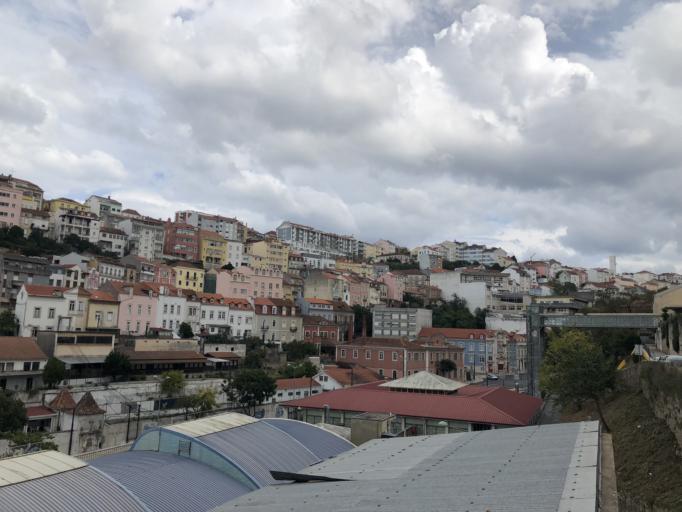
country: PT
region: Coimbra
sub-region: Coimbra
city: Coimbra
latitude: 40.2110
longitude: -8.4265
